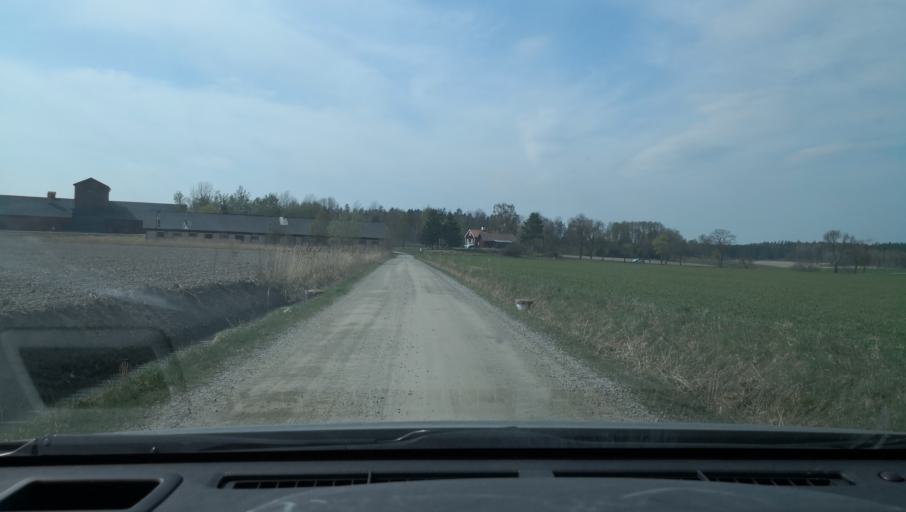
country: SE
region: Vaestmanland
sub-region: Vasteras
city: Skultuna
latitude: 59.7748
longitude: 16.3910
